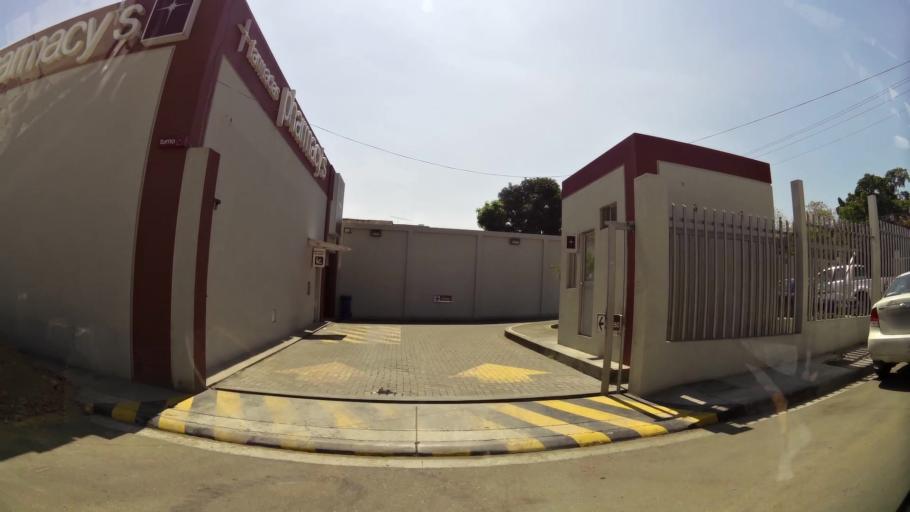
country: EC
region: Guayas
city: Guayaquil
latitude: -2.1643
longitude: -79.9121
